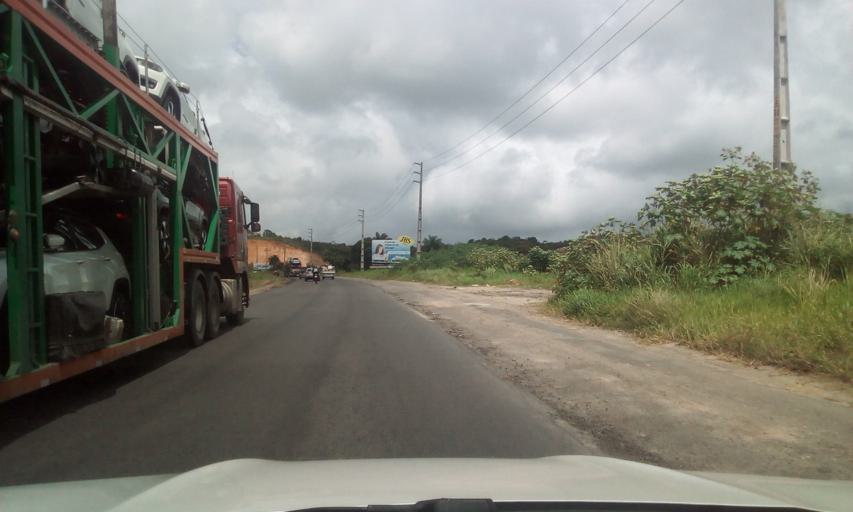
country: BR
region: Pernambuco
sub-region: Paulista
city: Paulista
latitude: -7.9791
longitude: -34.9289
